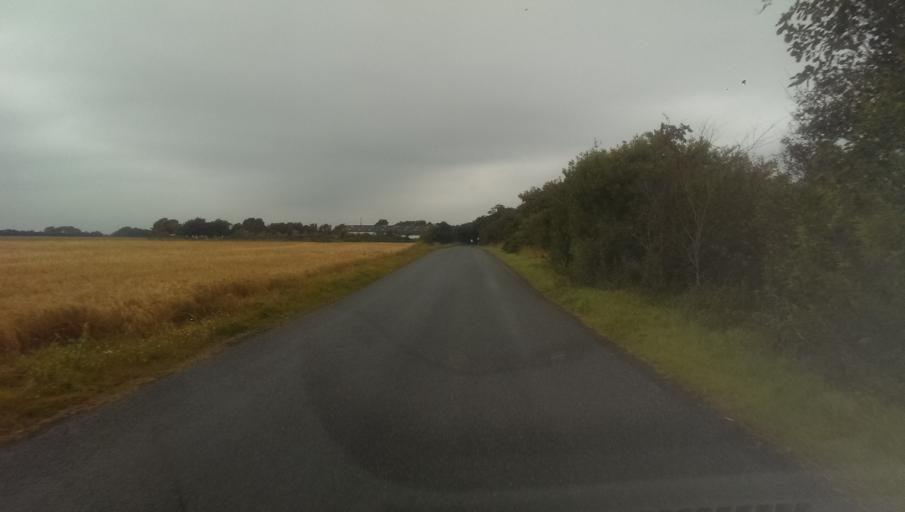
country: DK
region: South Denmark
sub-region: Esbjerg Kommune
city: Esbjerg
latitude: 55.5218
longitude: 8.4956
